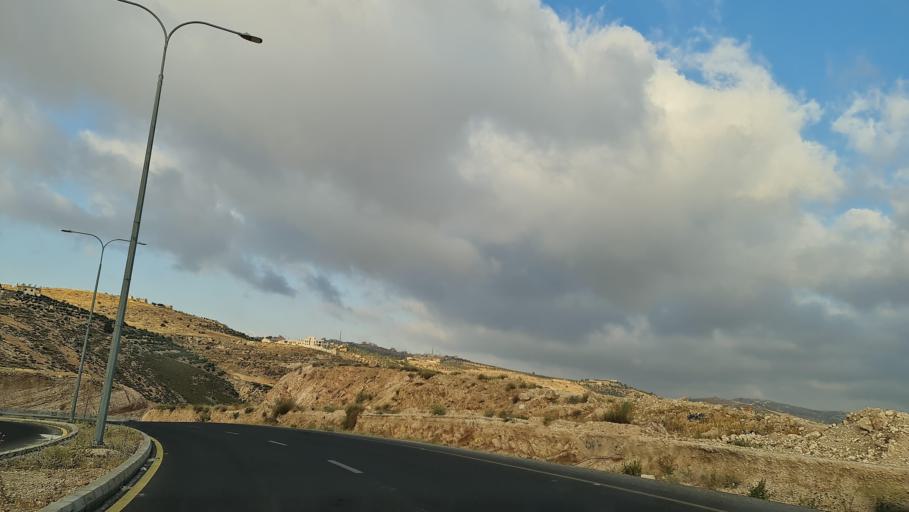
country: JO
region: Zarqa
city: Russeifa
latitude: 32.0920
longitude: 35.9622
